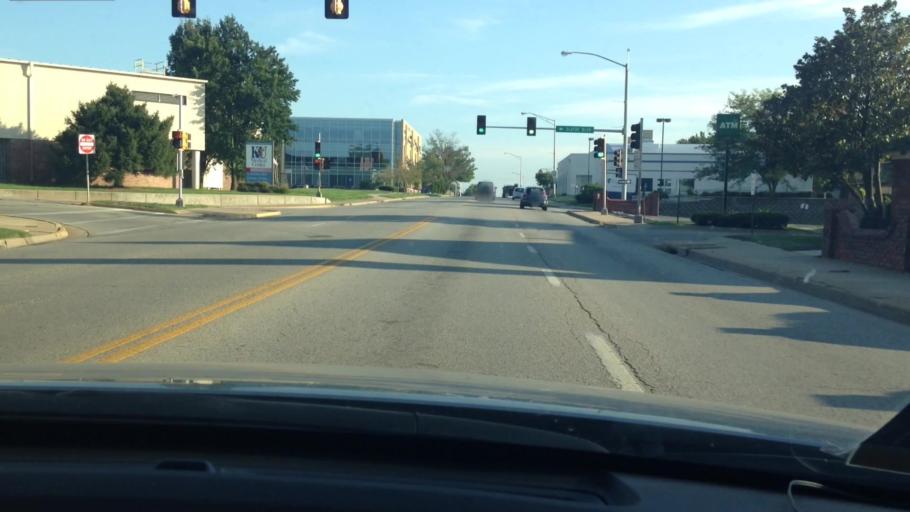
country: US
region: Kansas
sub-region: Johnson County
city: Westwood
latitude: 39.0543
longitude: -94.6119
